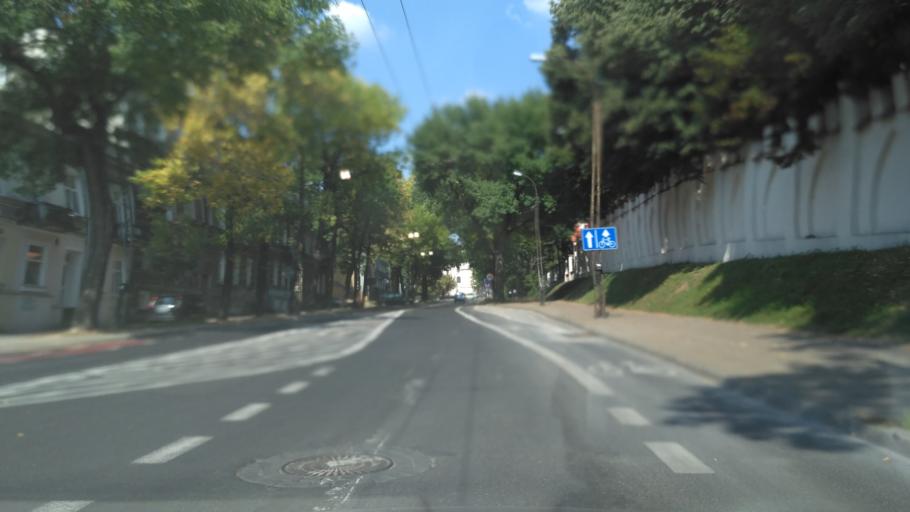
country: PL
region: Lublin Voivodeship
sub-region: Powiat lubelski
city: Lublin
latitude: 51.2432
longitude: 22.5688
